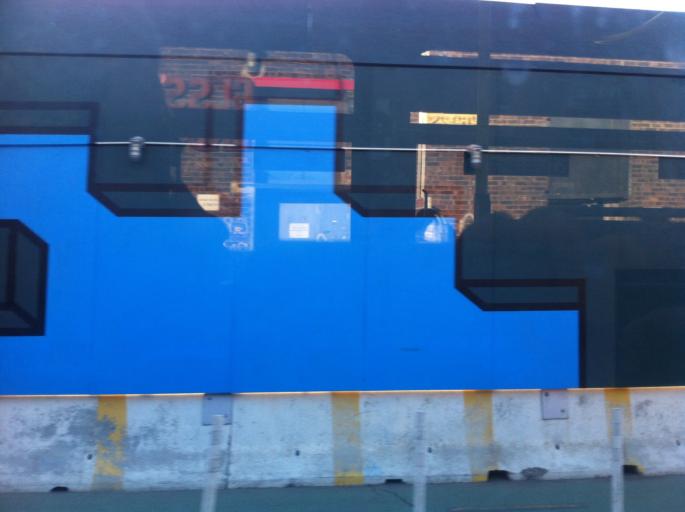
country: US
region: New York
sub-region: Queens County
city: Long Island City
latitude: 40.7151
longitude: -73.9667
